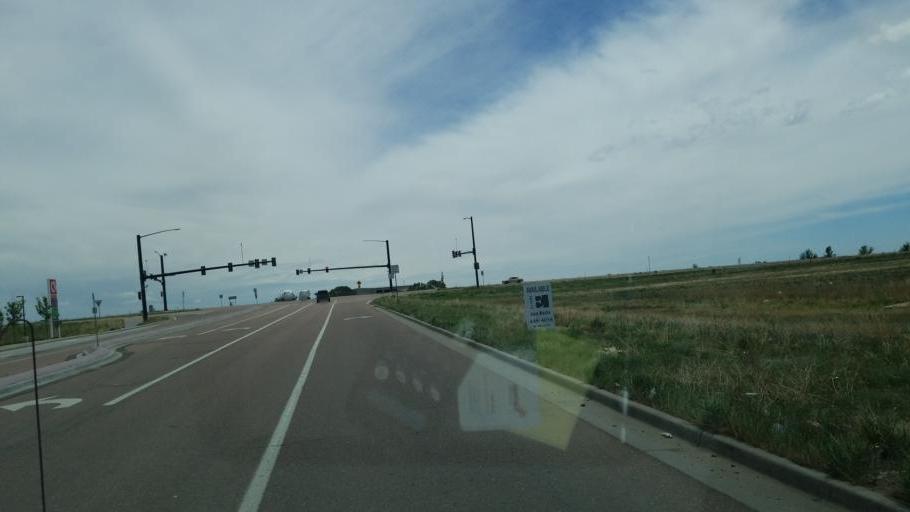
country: US
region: Colorado
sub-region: El Paso County
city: Cimarron Hills
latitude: 38.8441
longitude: -104.6923
